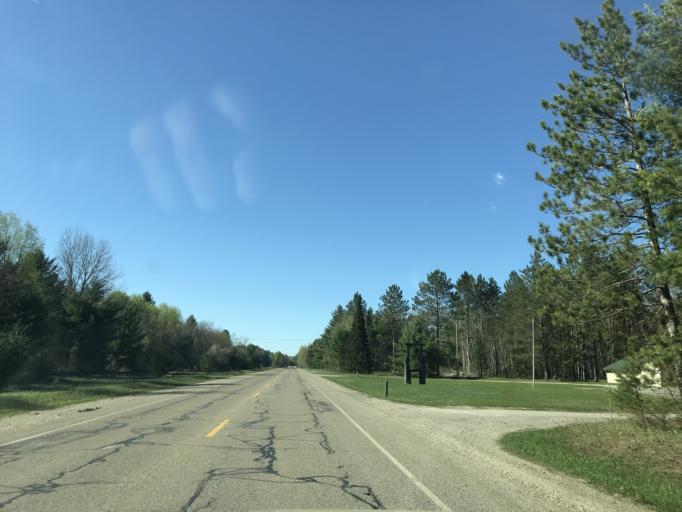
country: US
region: Michigan
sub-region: Crawford County
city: Grayling
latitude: 44.7534
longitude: -84.7525
